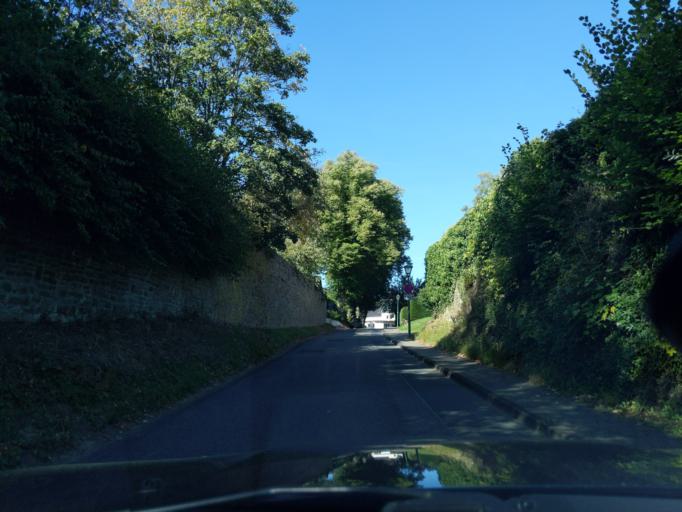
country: DE
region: North Rhine-Westphalia
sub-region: Regierungsbezirk Koln
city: Eitorf
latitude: 50.7651
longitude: 7.3964
